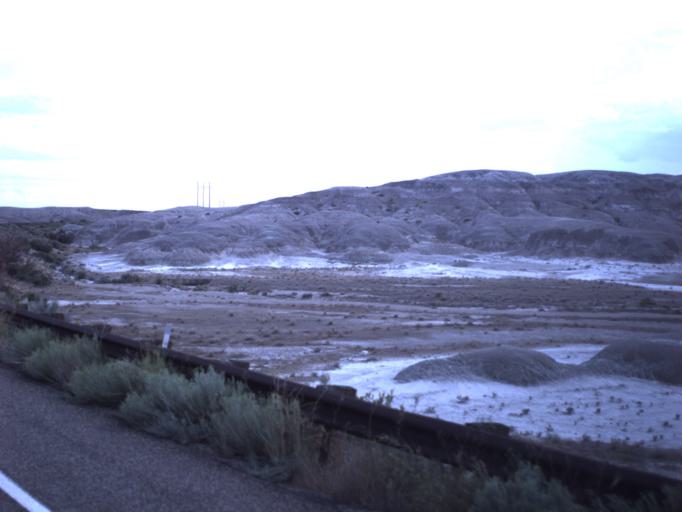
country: US
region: Utah
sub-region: Uintah County
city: Naples
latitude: 40.1075
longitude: -109.2263
